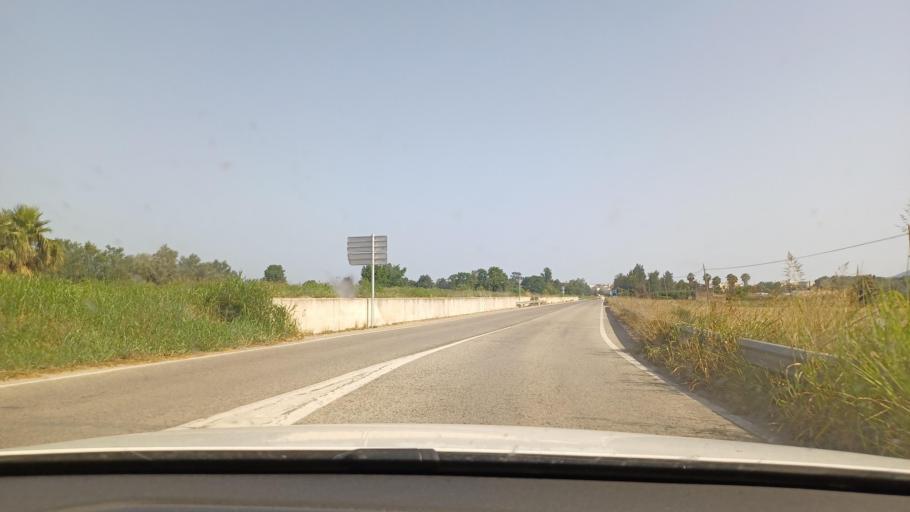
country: ES
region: Catalonia
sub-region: Provincia de Tarragona
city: Amposta
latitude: 40.7260
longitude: 0.5718
